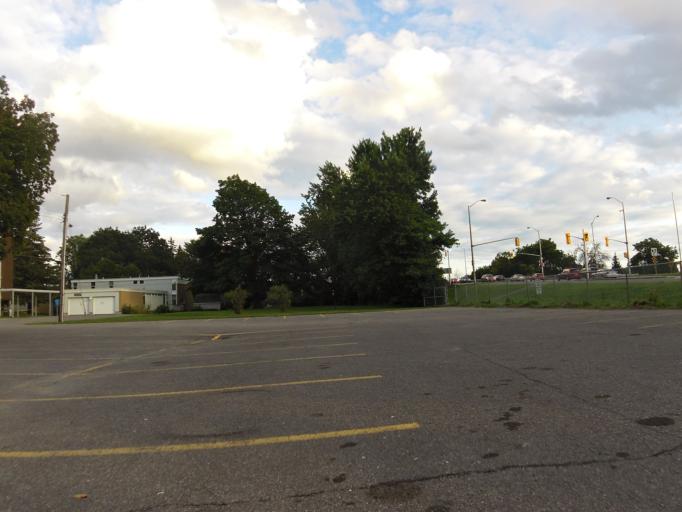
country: CA
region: Ontario
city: Ottawa
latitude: 45.3722
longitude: -75.7552
